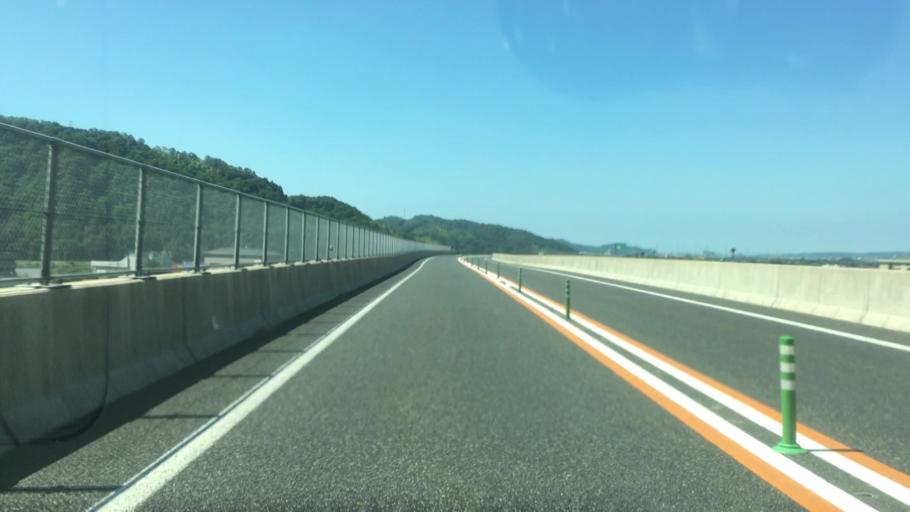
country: JP
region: Tottori
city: Tottori
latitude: 35.4163
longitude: 134.2062
